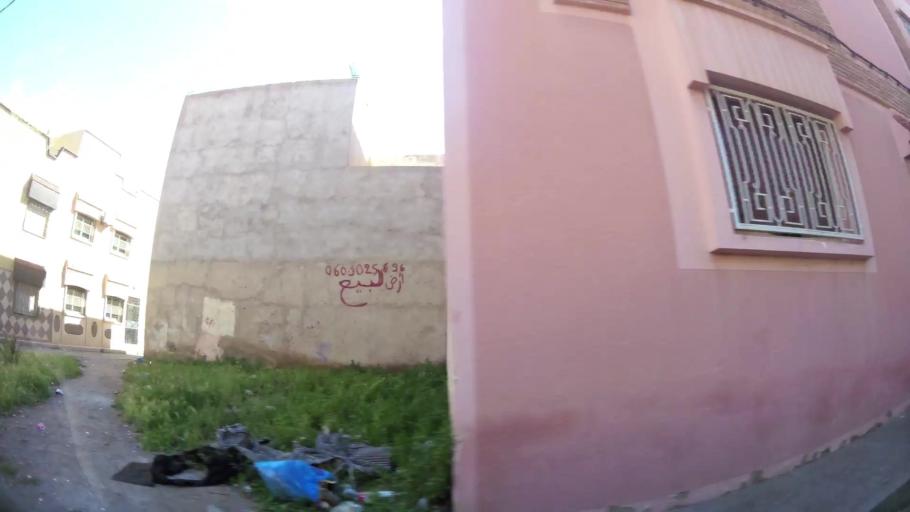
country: MA
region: Oriental
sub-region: Oujda-Angad
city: Oujda
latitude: 34.6550
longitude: -1.8959
